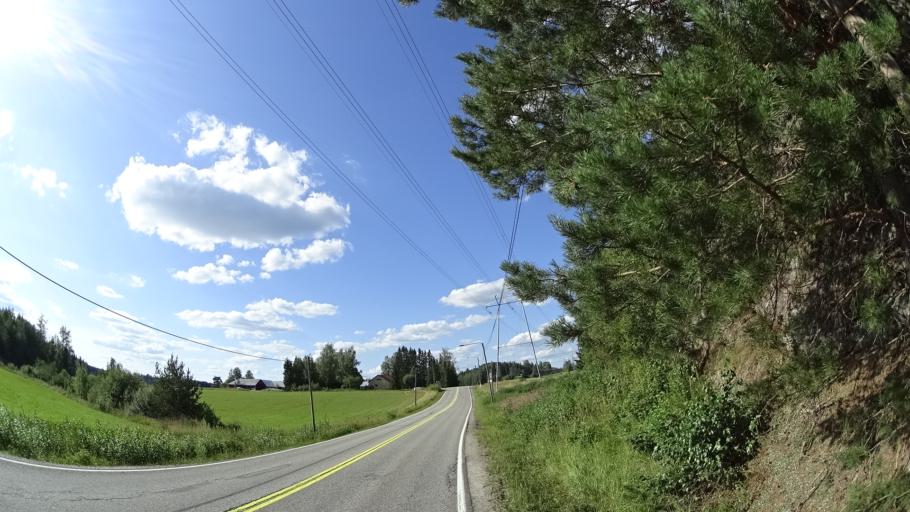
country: FI
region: Uusimaa
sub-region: Helsinki
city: Vihti
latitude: 60.3774
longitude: 24.3582
